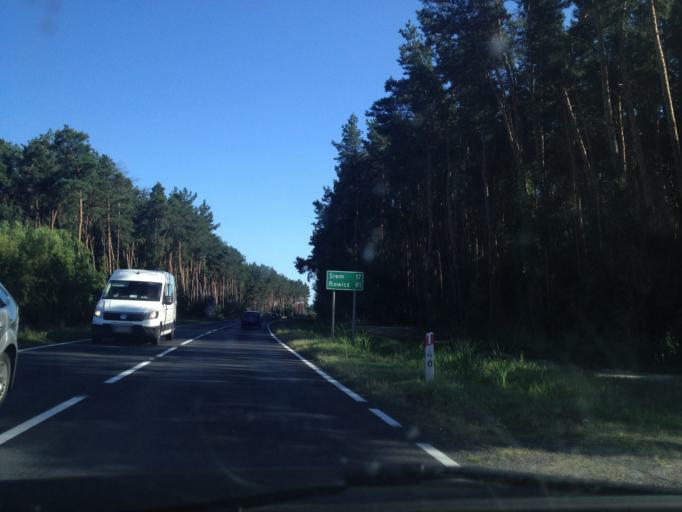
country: PL
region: Greater Poland Voivodeship
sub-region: Powiat poznanski
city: Kornik
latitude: 52.2245
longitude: 17.0724
